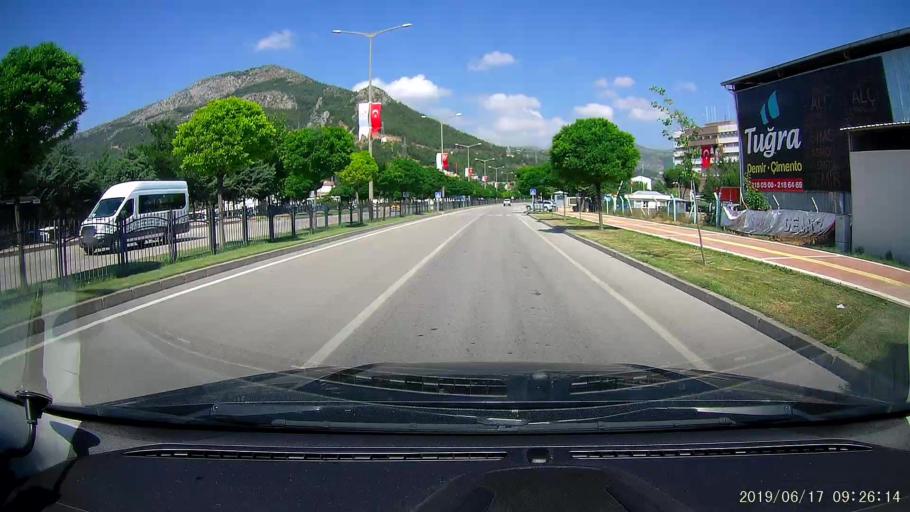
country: TR
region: Amasya
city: Amasya
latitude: 40.6686
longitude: 35.8385
